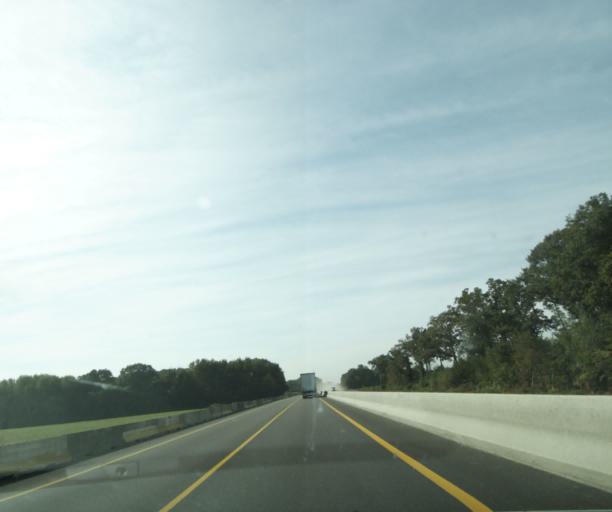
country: FR
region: Bourgogne
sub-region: Departement de Saone-et-Loire
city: Paray-le-Monial
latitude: 46.4899
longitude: 4.1542
